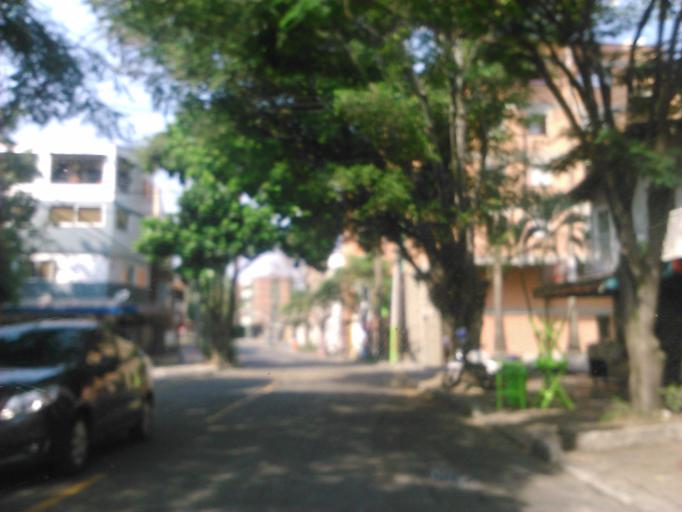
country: CO
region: Antioquia
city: Medellin
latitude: 6.2514
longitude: -75.6084
